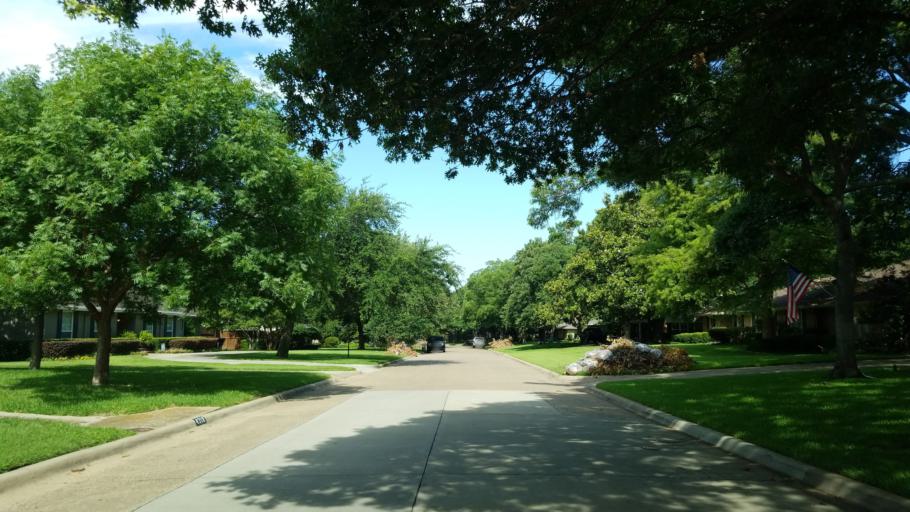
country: US
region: Texas
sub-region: Dallas County
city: Addison
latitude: 32.9072
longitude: -96.8353
